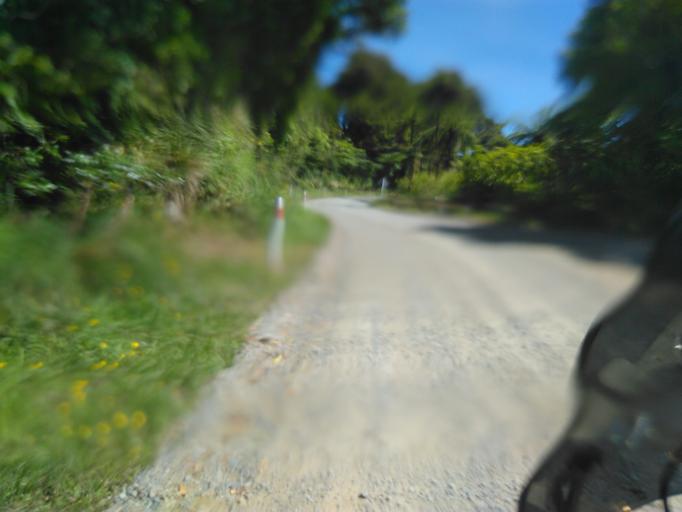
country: NZ
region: Hawke's Bay
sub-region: Wairoa District
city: Wairoa
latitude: -38.7965
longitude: 177.1251
